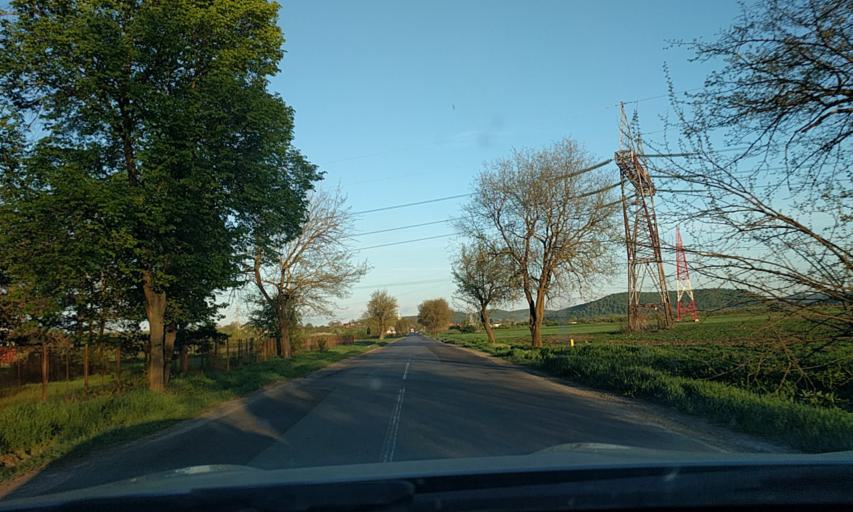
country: RO
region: Mures
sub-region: Comuna Ungheni
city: Ungheni
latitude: 46.4754
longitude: 24.4732
